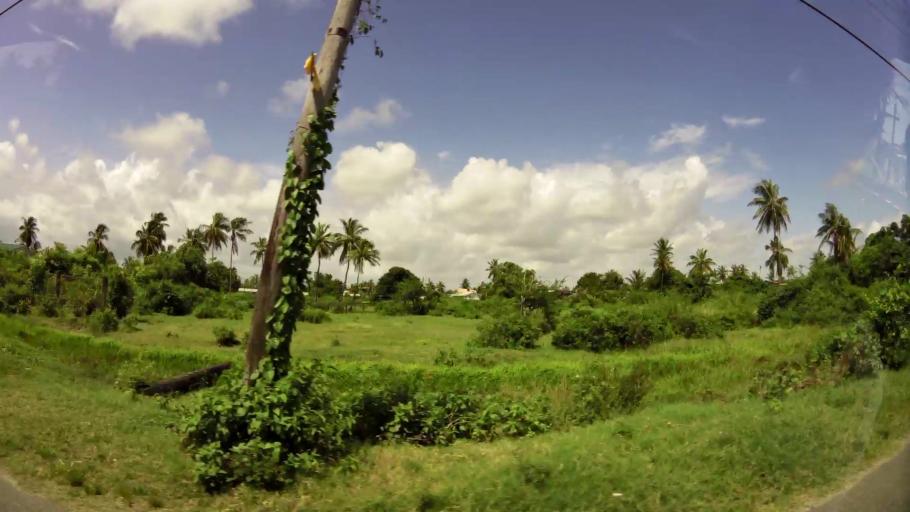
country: GY
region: Demerara-Mahaica
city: Mahaica Village
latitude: 6.7681
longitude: -58.0008
